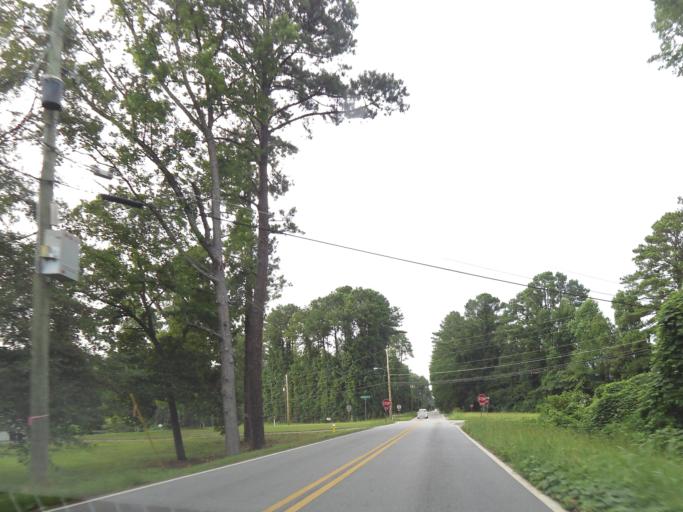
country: US
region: Georgia
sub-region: Bibb County
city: West Point
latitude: 32.8987
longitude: -83.7745
